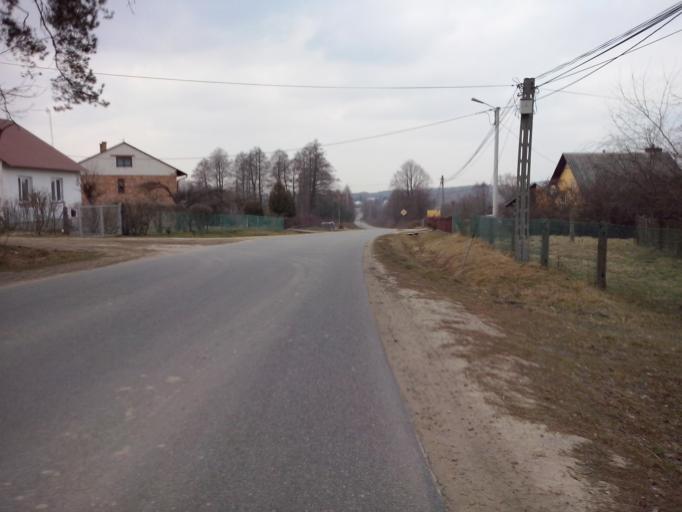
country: PL
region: Subcarpathian Voivodeship
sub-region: Powiat nizanski
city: Krzeszow
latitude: 50.4166
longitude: 22.3337
